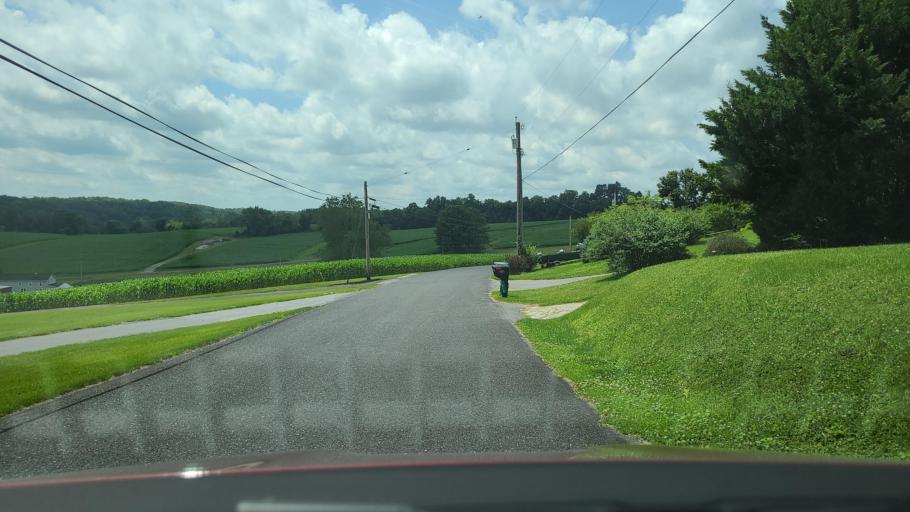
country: US
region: Maryland
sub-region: Carroll County
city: Westminster
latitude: 39.5454
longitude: -77.0238
